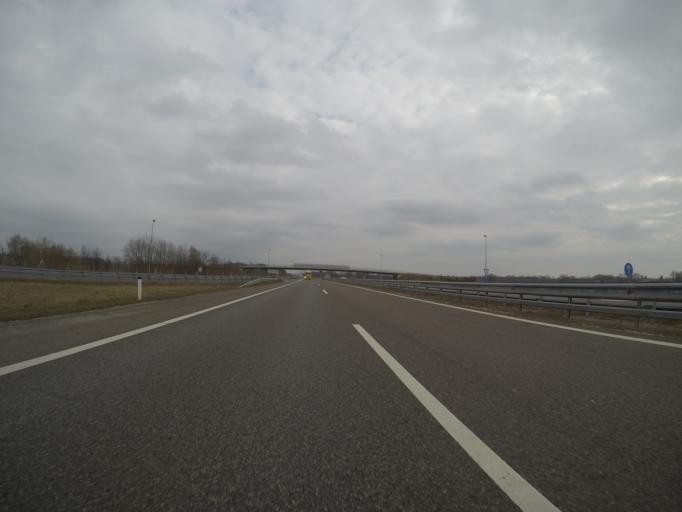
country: SI
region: Turnisce
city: Turnisce
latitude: 46.6102
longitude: 16.3174
